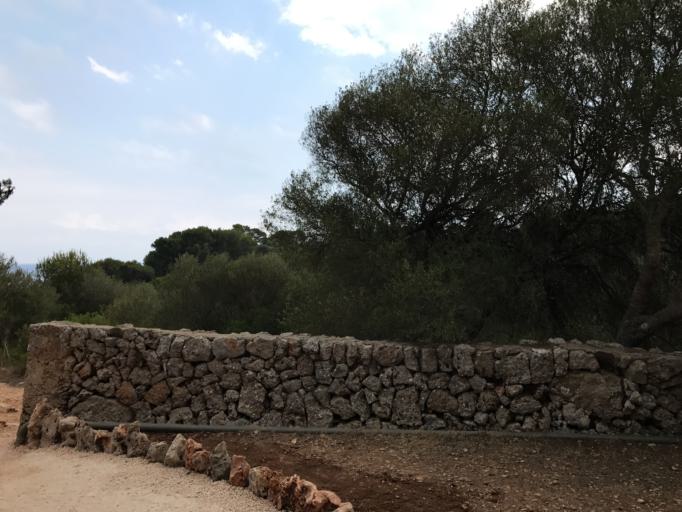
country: ES
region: Balearic Islands
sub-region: Illes Balears
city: Sant Llorenc des Cardassar
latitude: 39.5332
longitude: 3.3313
